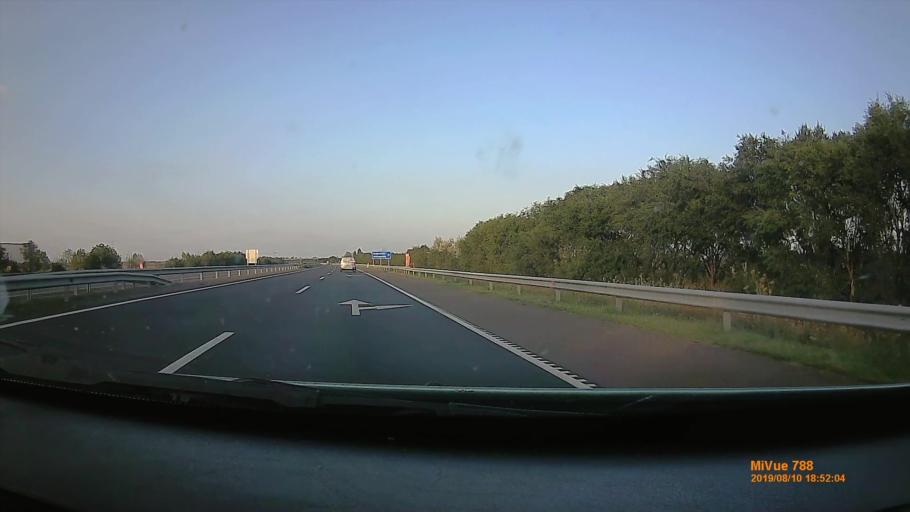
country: HU
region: Borsod-Abauj-Zemplen
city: Mezokeresztes
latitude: 47.8091
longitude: 20.7035
